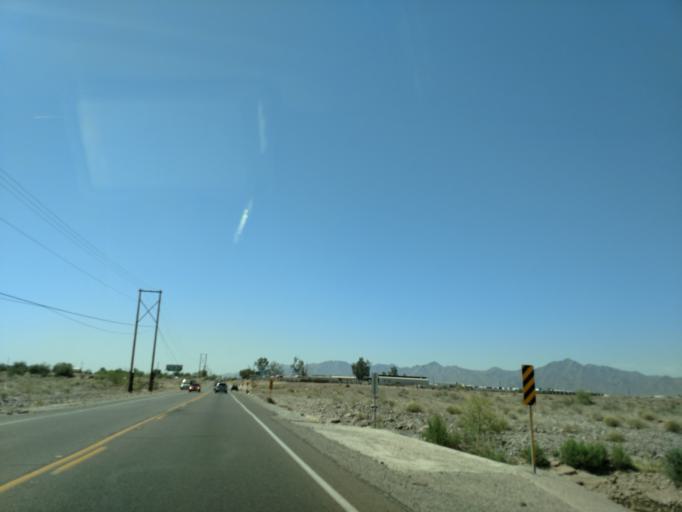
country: US
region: Arizona
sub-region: Maricopa County
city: Laveen
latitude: 33.3980
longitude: -112.2037
